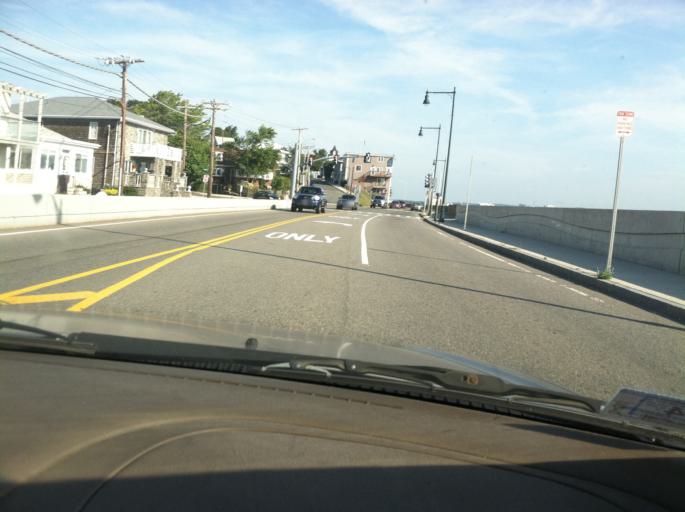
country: US
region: Massachusetts
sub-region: Suffolk County
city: Winthrop
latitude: 42.3921
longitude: -70.9814
